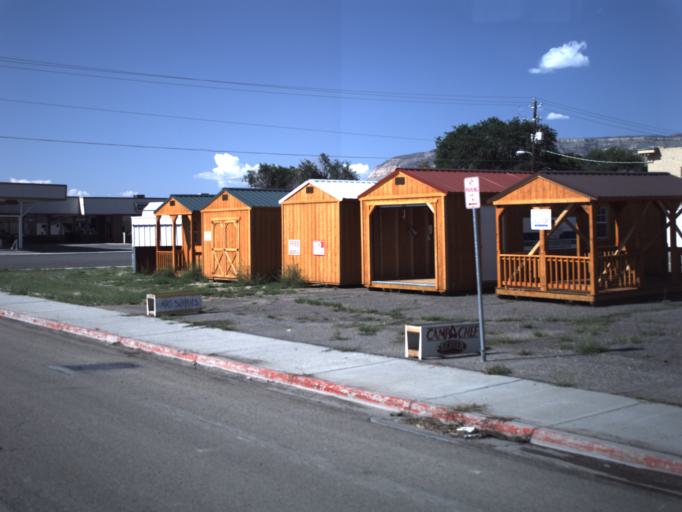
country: US
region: Utah
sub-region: Emery County
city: Ferron
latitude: 39.0906
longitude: -111.1321
